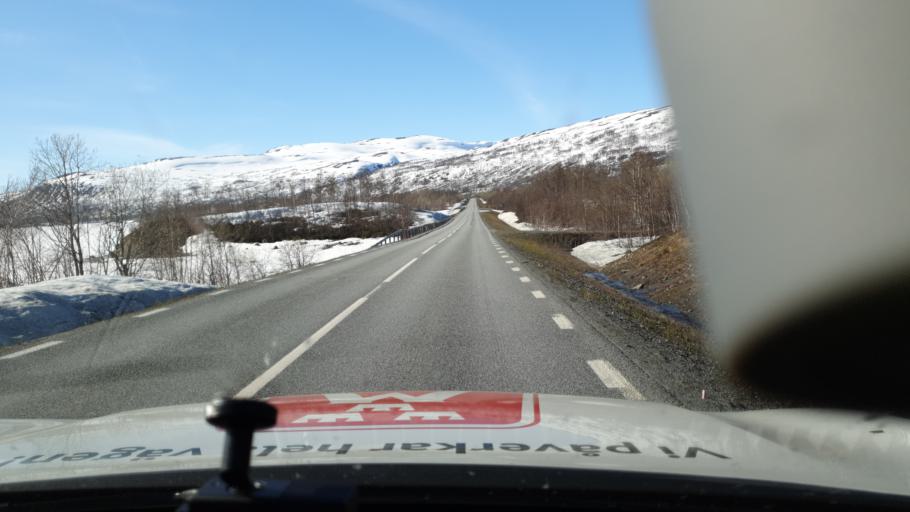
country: NO
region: Nordland
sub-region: Rana
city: Mo i Rana
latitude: 66.1105
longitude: 14.8148
